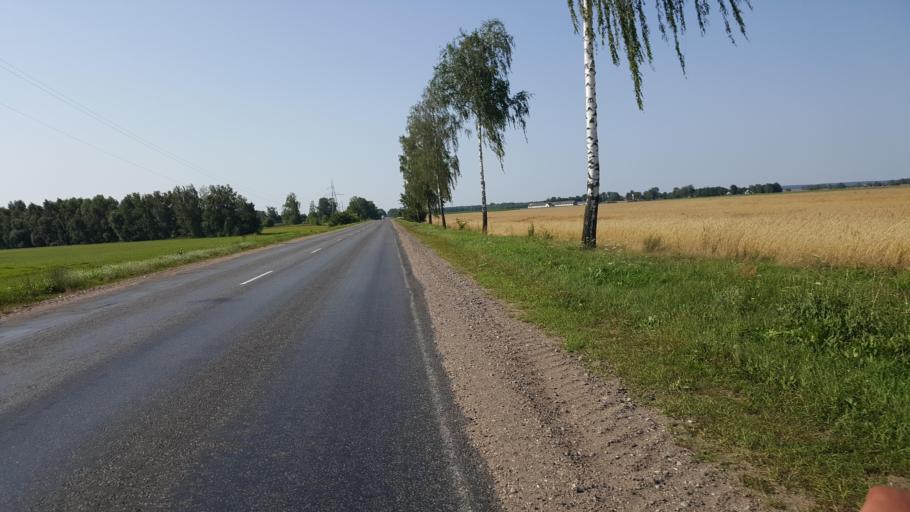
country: BY
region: Brest
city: Zhabinka
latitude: 52.2499
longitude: 23.9705
